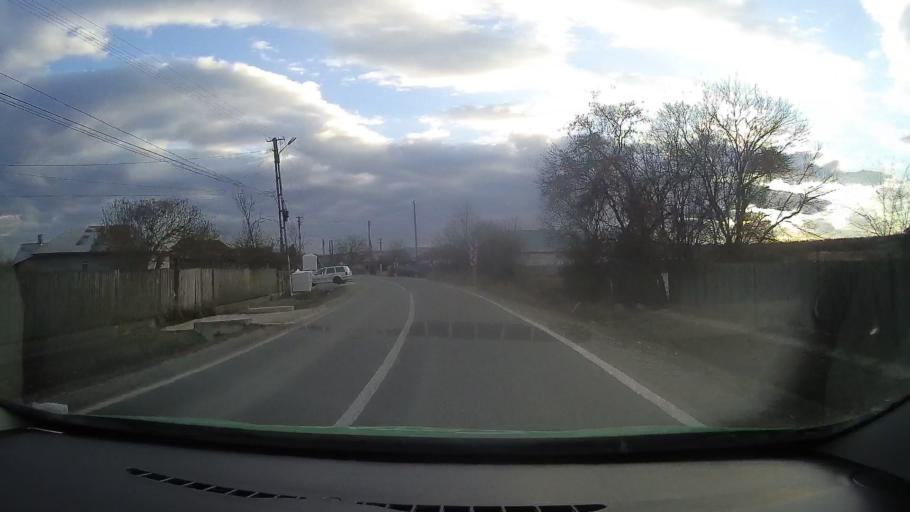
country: RO
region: Dambovita
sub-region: Comuna I. L. Caragiale
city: Mija
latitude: 44.9227
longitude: 25.6898
